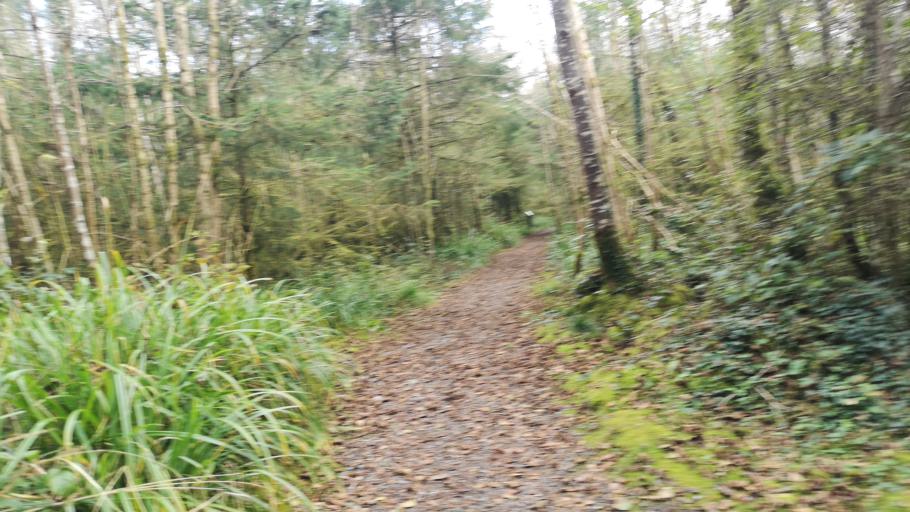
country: IE
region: Connaught
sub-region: County Galway
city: Loughrea
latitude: 53.2374
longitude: -8.6499
